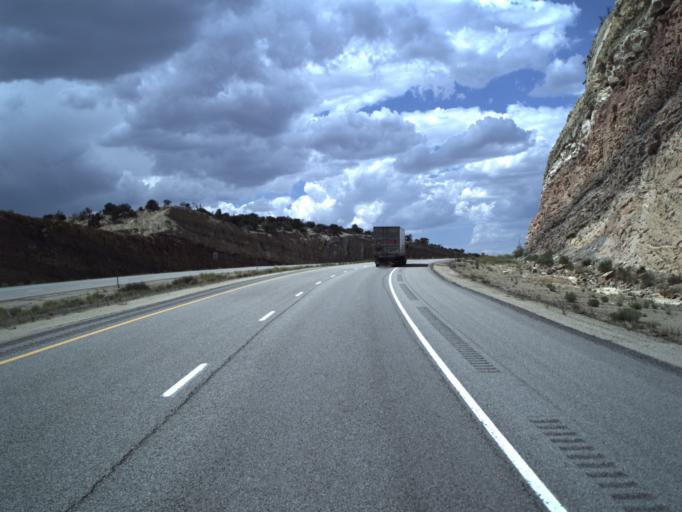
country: US
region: Utah
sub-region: Emery County
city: Ferron
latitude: 38.8487
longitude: -110.9018
